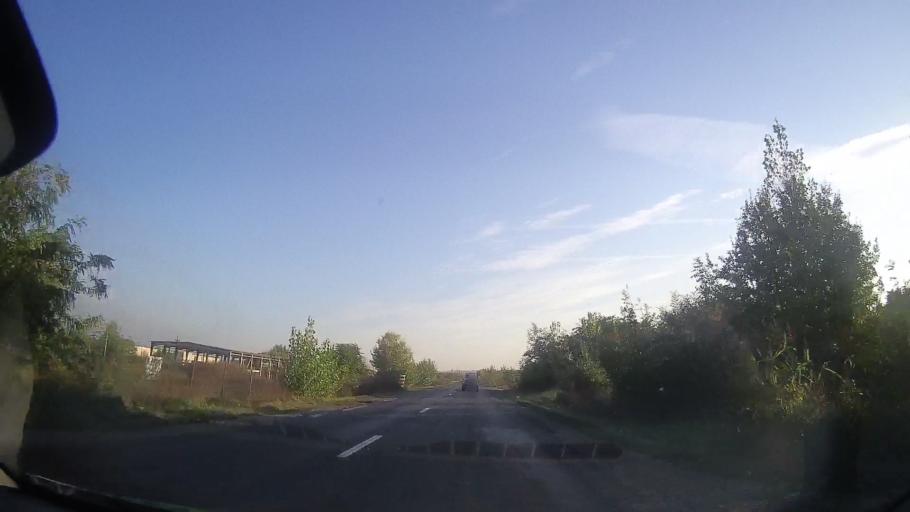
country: RO
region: Timis
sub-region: Comuna Ghiroda
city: Giarmata-Vii
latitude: 45.8199
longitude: 21.2706
